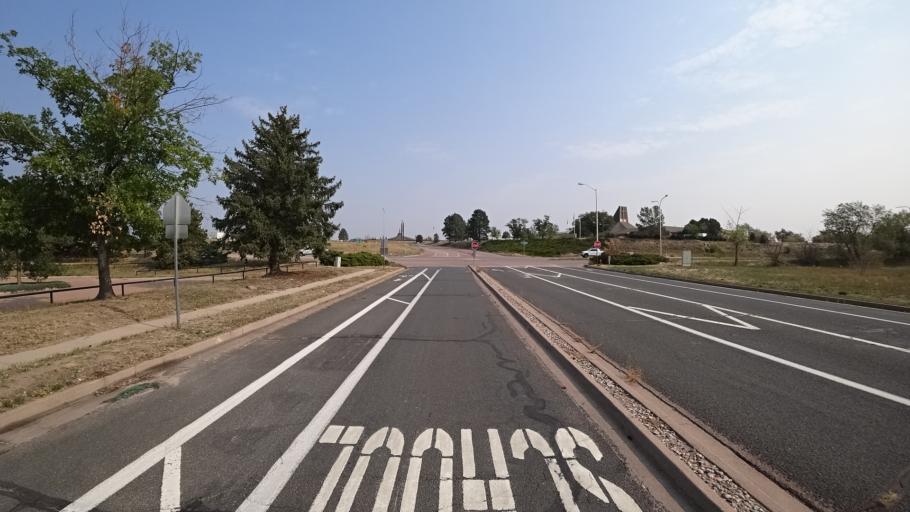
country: US
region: Colorado
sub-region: El Paso County
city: Stratmoor
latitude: 38.8130
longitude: -104.7529
